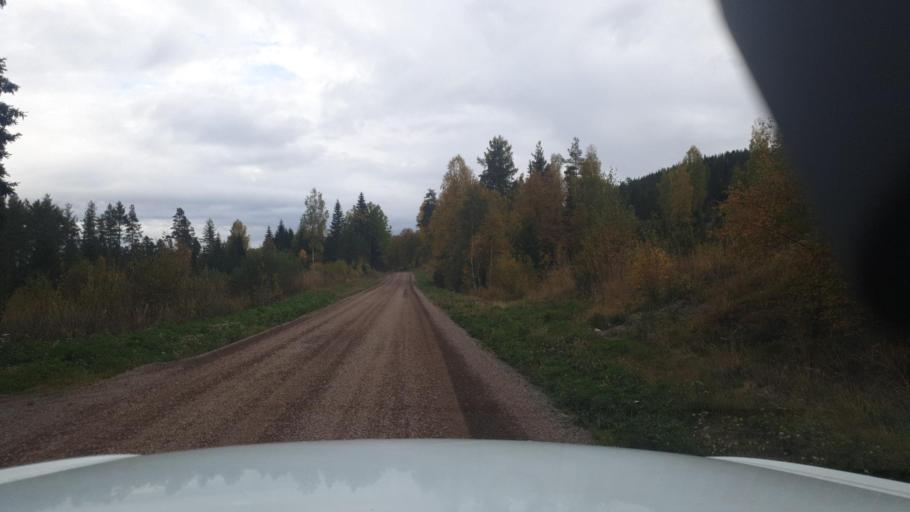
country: SE
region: Vaermland
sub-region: Eda Kommun
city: Charlottenberg
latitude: 60.0794
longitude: 12.5240
